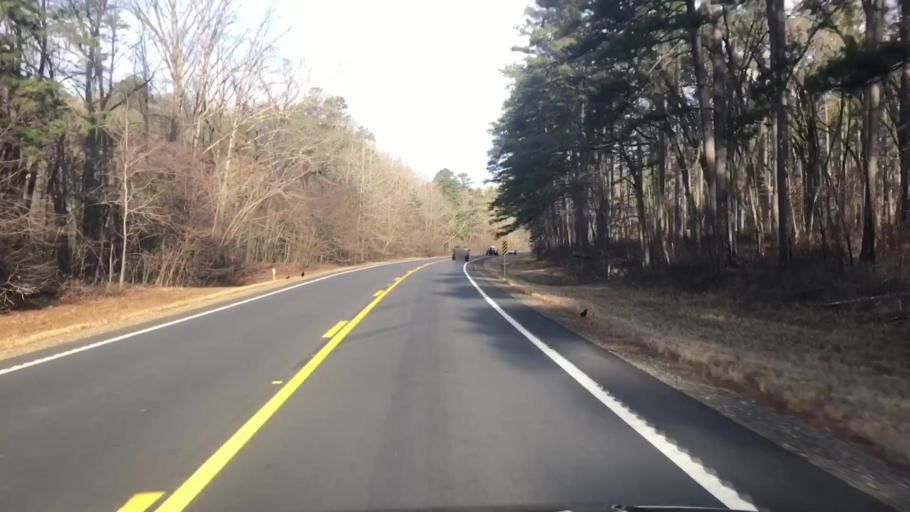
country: US
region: Arkansas
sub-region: Montgomery County
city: Mount Ida
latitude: 34.5188
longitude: -93.3877
